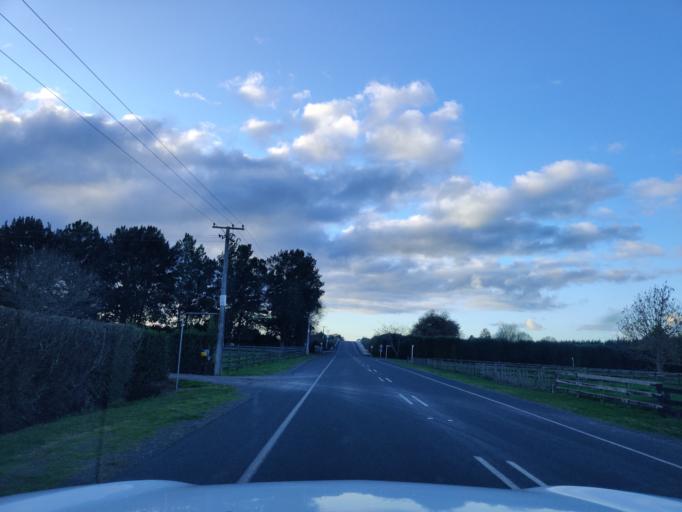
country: NZ
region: Waikato
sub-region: Waipa District
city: Cambridge
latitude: -37.8720
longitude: 175.4389
